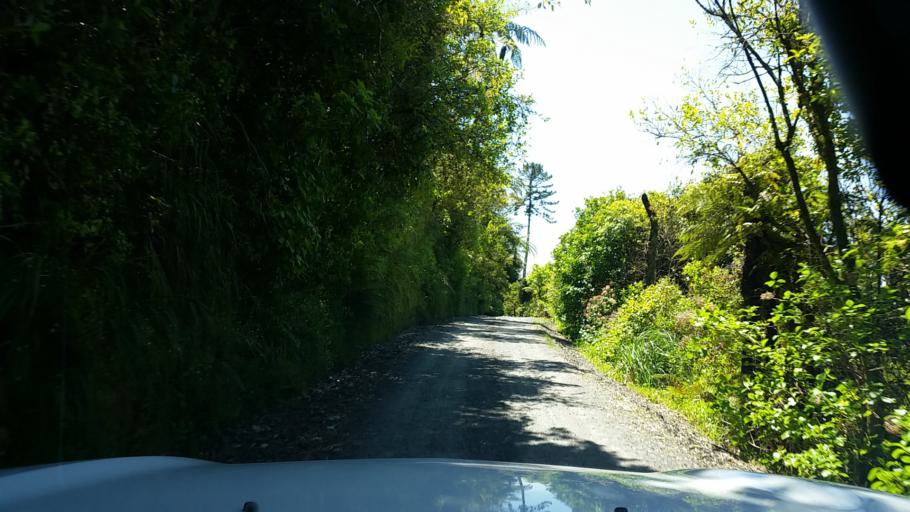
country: NZ
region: Auckland
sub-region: Auckland
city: Titirangi
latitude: -36.9296
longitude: 174.5810
